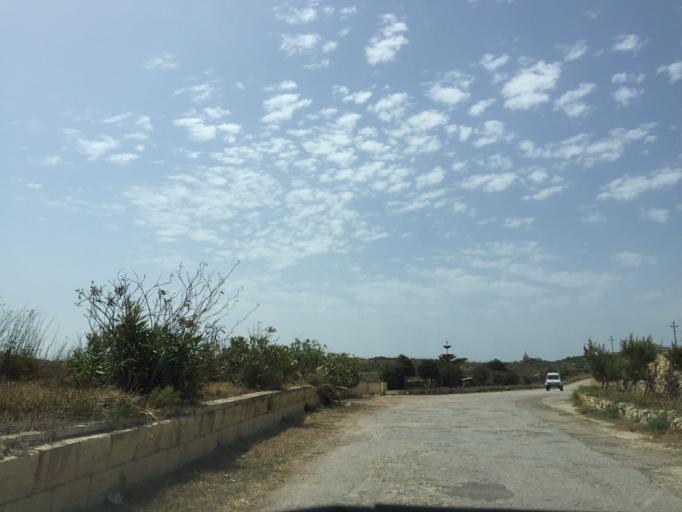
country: MT
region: In-Nadur
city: Nadur
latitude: 36.0545
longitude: 14.2944
